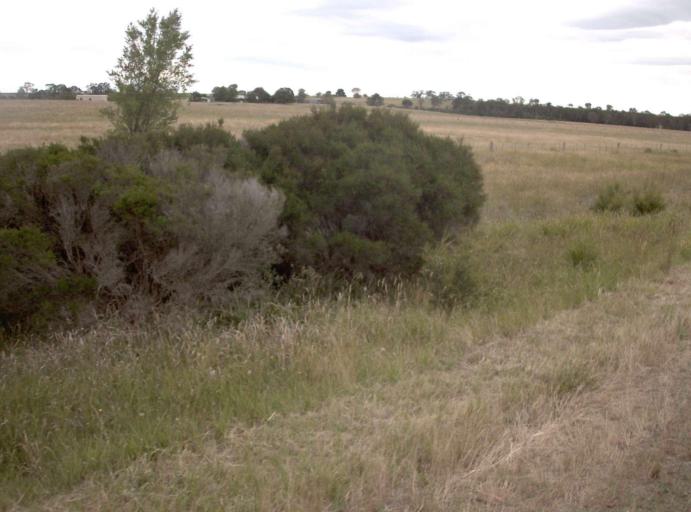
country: AU
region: Victoria
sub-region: East Gippsland
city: Bairnsdale
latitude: -37.9880
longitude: 147.3986
